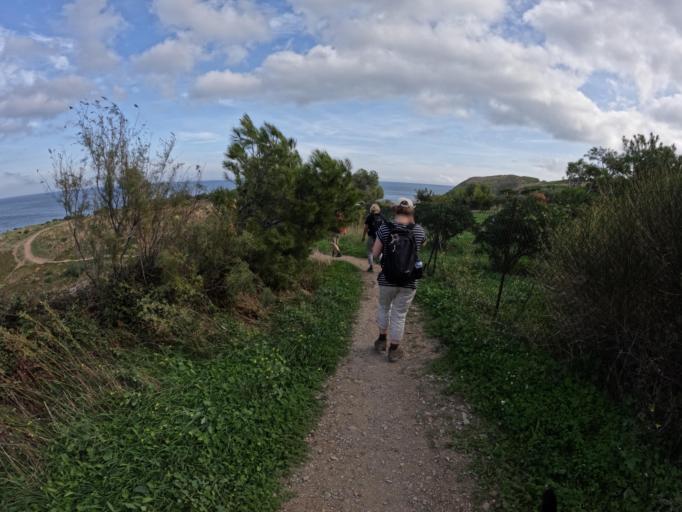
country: FR
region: Languedoc-Roussillon
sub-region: Departement des Pyrenees-Orientales
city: Cervera de la Marenda
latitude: 42.4584
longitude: 3.1609
